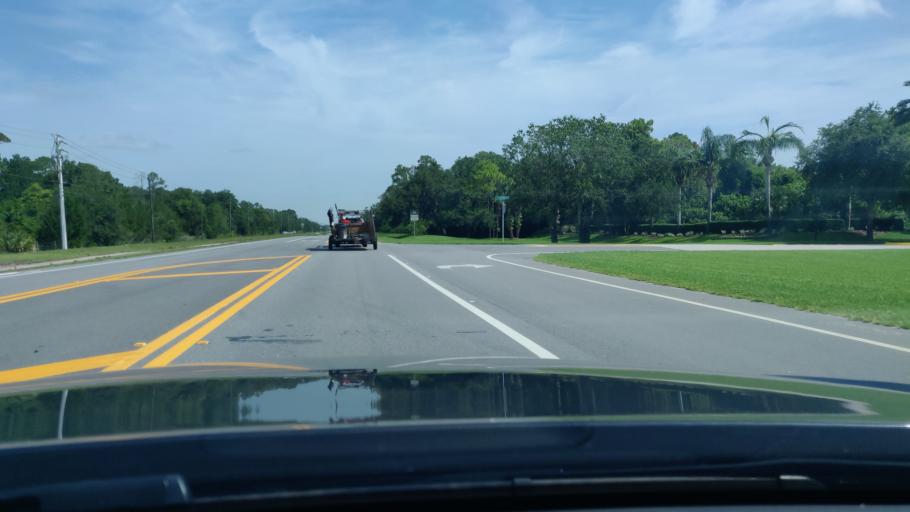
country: US
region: Florida
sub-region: Flagler County
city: Flagler Beach
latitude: 29.5052
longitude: -81.1599
